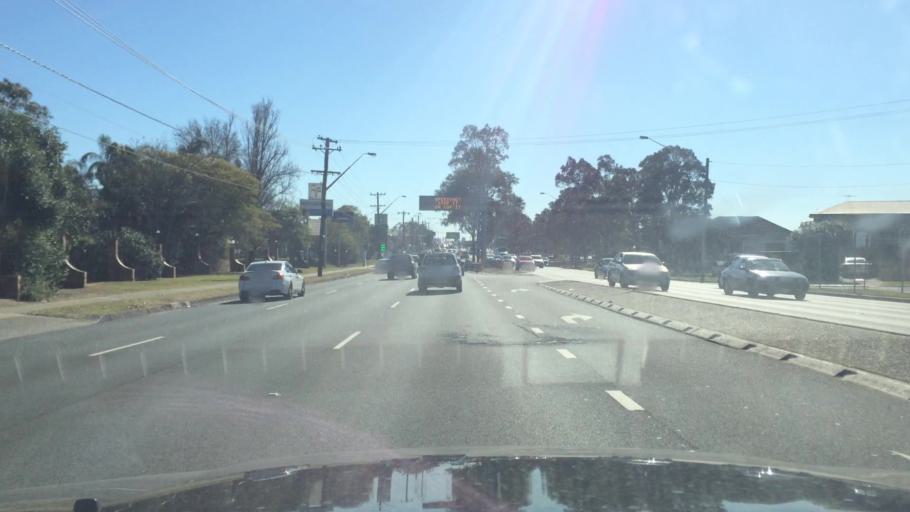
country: AU
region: New South Wales
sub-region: Campbelltown Municipality
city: Glenfield
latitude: -33.9426
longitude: 150.9115
